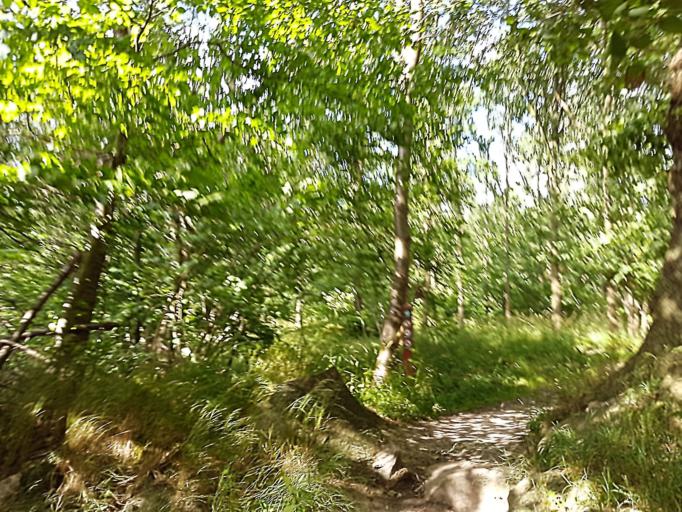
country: DK
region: Capital Region
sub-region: Egedal Kommune
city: Ganlose
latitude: 55.7972
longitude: 12.2909
